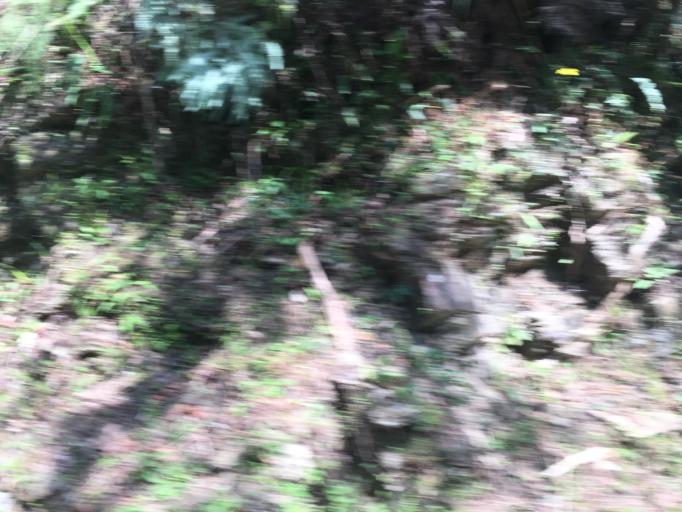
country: TW
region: Taiwan
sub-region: Yilan
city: Yilan
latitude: 24.7551
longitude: 121.6212
